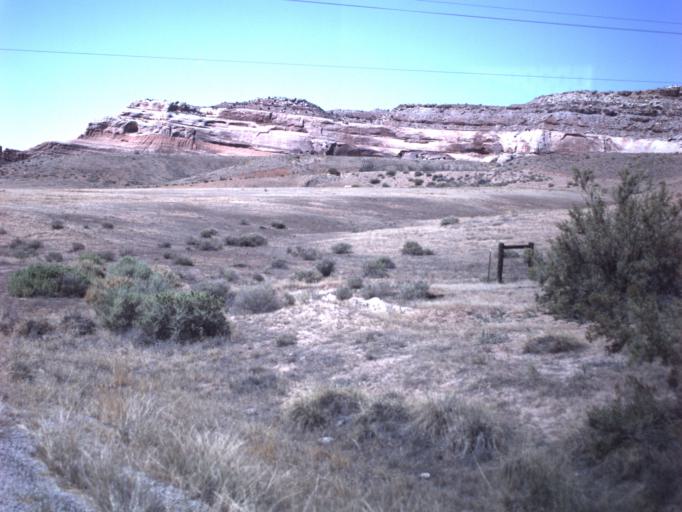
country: US
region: Utah
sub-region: Grand County
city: Moab
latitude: 38.8138
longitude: -109.3013
